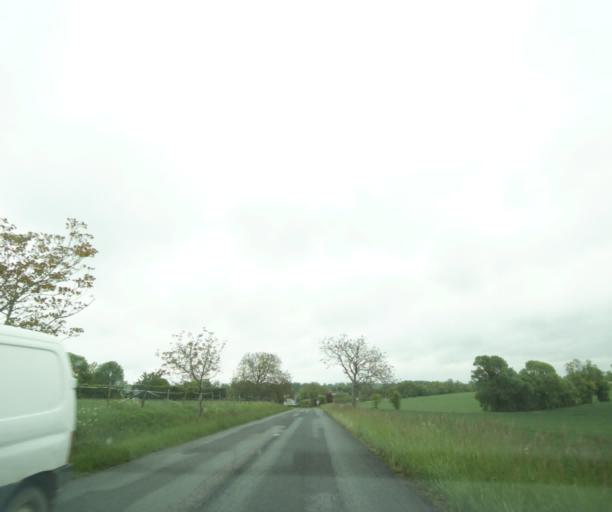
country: FR
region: Poitou-Charentes
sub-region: Departement de la Charente-Maritime
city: Pons
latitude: 45.6428
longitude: -0.5581
